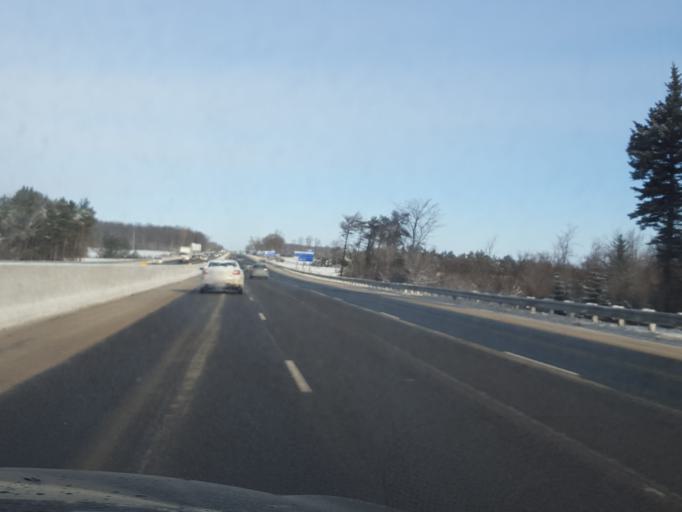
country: CA
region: Ontario
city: Innisfil
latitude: 44.2582
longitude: -79.6724
